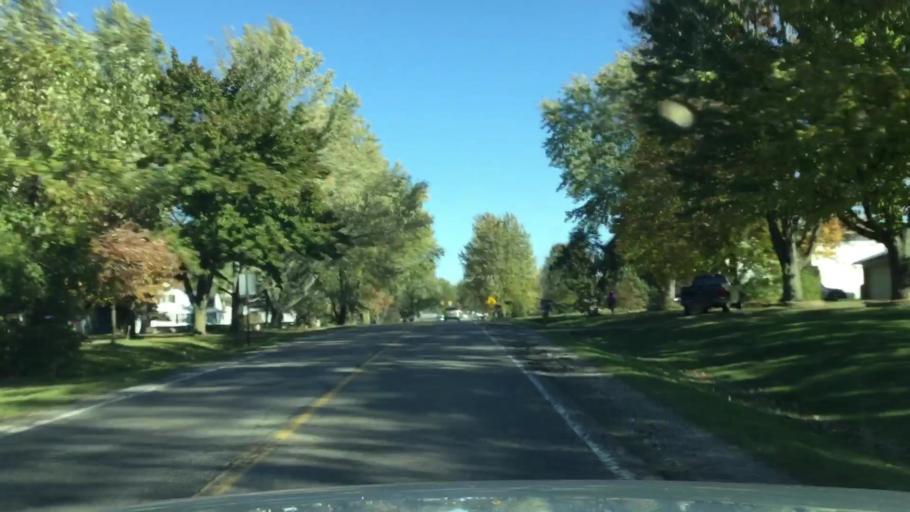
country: US
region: Michigan
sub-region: Lapeer County
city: Lapeer
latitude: 43.0725
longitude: -83.3215
